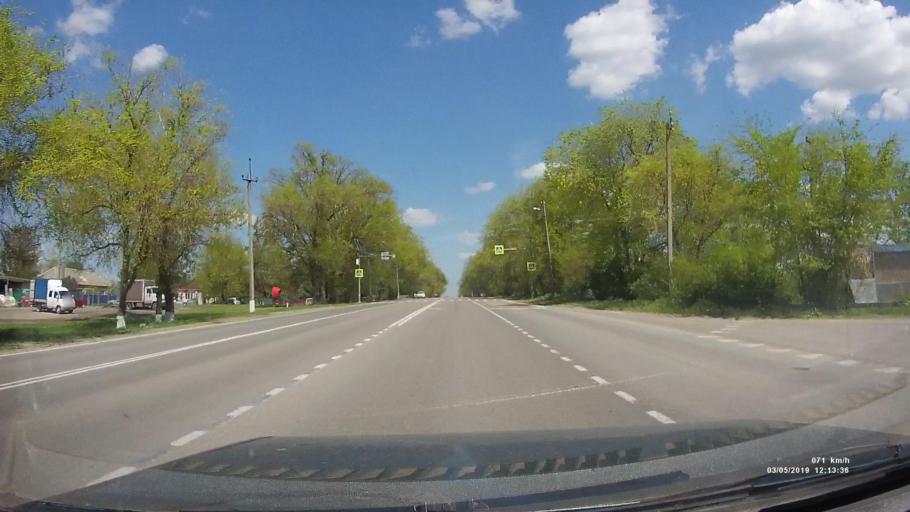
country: RU
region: Rostov
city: Melikhovskaya
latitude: 47.3344
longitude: 40.5562
